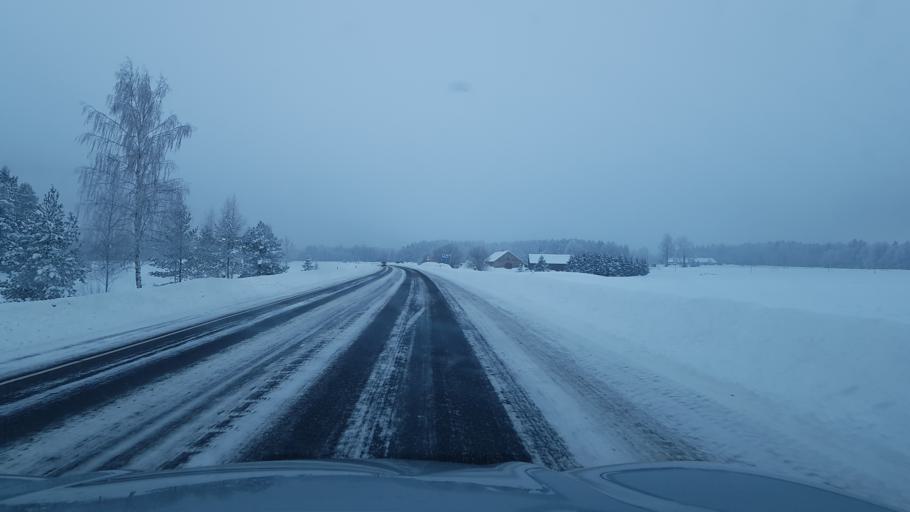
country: EE
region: Ida-Virumaa
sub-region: Johvi vald
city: Johvi
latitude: 59.2306
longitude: 27.3411
